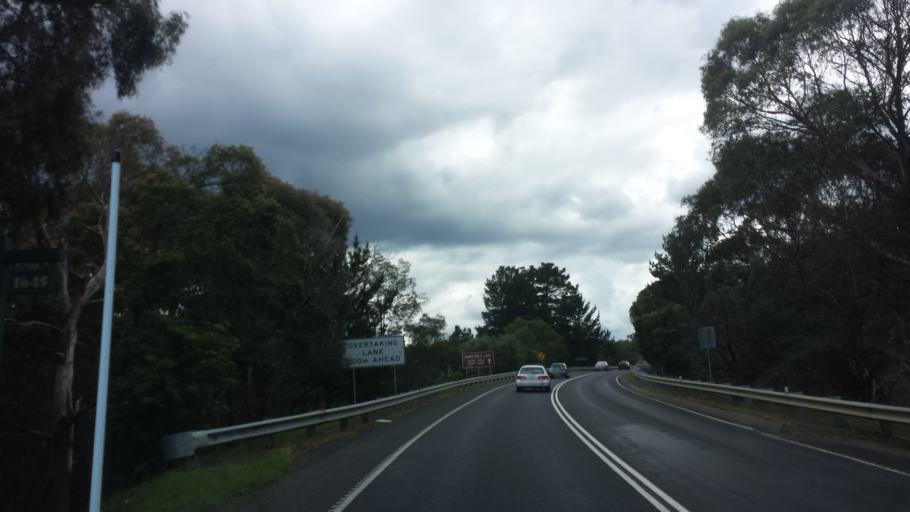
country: AU
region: Victoria
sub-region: Yarra Ranges
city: Selby
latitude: -37.9397
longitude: 145.3828
